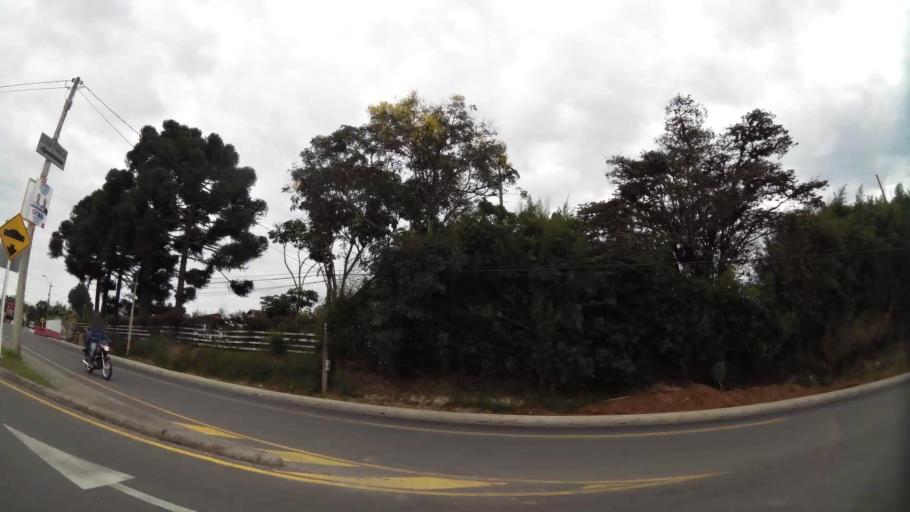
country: CO
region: Antioquia
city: Rionegro
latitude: 6.1529
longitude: -75.4124
